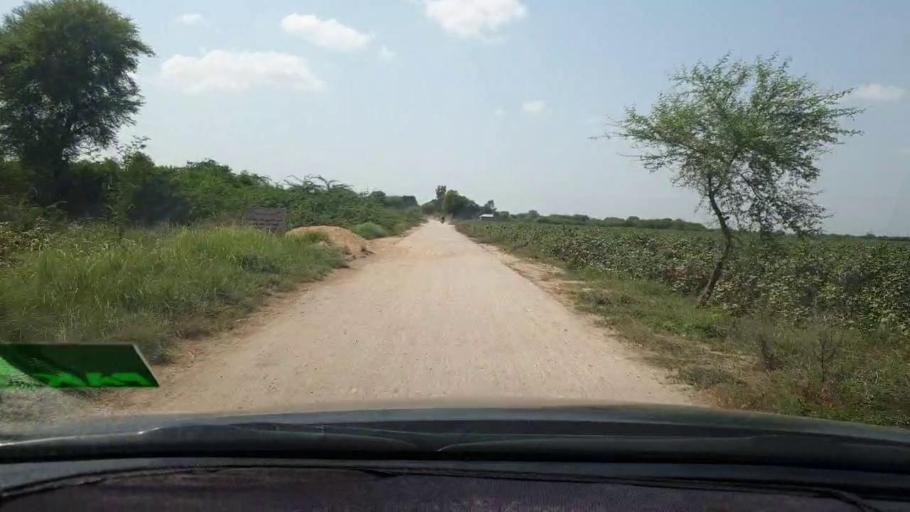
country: PK
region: Sindh
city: Naukot
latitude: 24.9150
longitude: 69.2637
